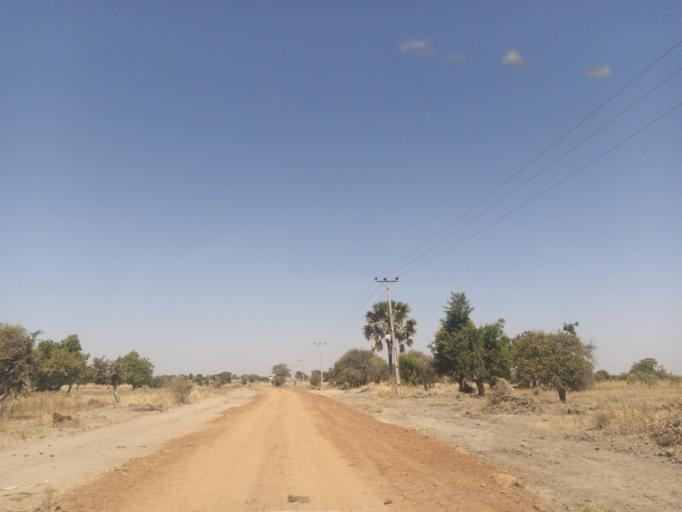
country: NG
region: Adamawa
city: Yola
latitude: 9.3046
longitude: 12.8897
